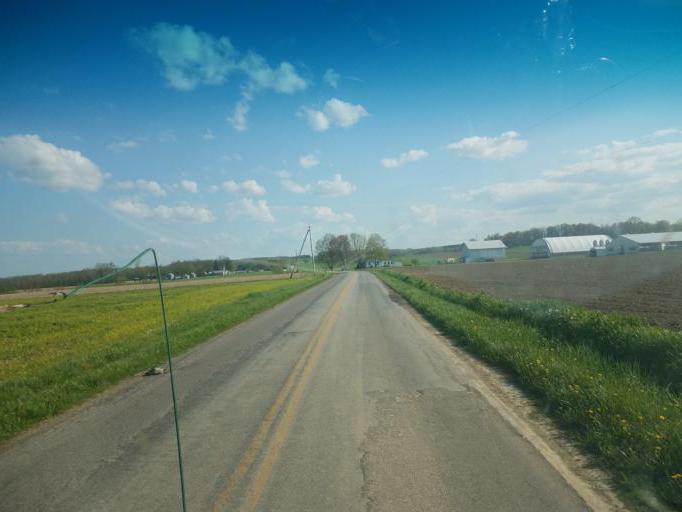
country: US
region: Ohio
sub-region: Wayne County
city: Apple Creek
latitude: 40.7709
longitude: -81.8793
